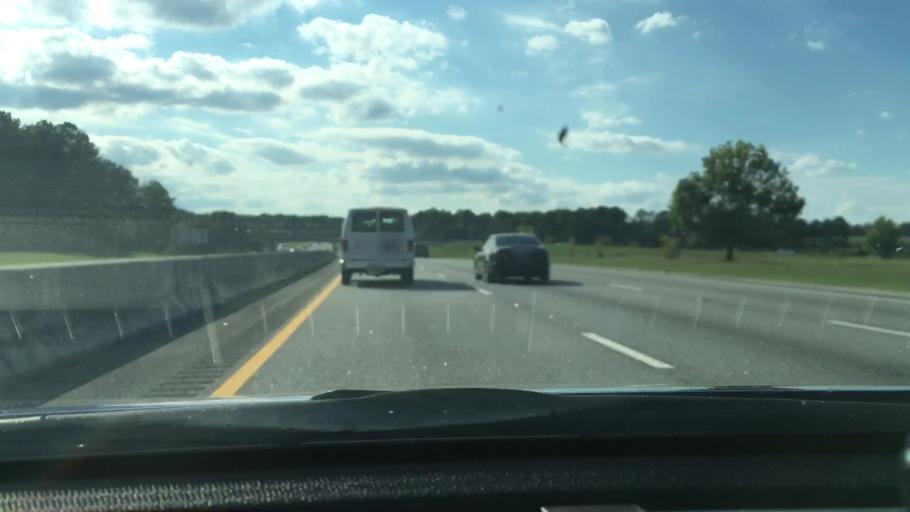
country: US
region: South Carolina
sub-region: Richland County
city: Dentsville
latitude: 34.0740
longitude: -80.9665
